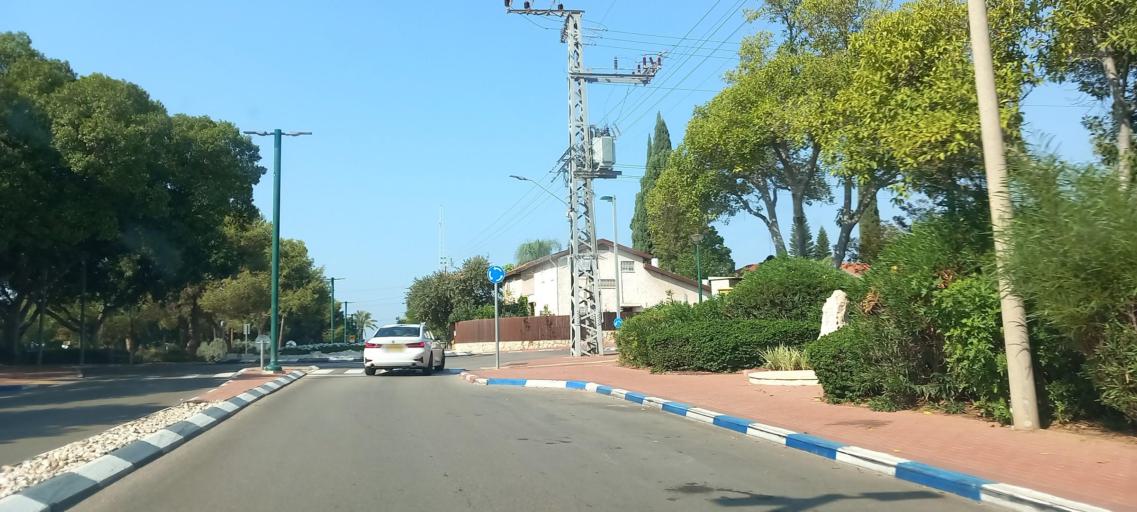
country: IL
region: Tel Aviv
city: Or Yehuda
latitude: 32.0465
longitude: 34.8353
